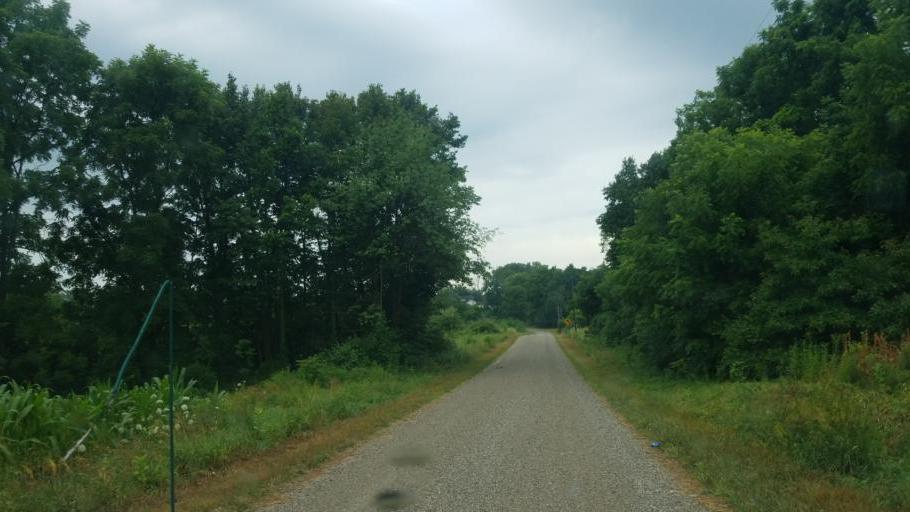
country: US
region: Indiana
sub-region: Steuben County
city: Hamilton
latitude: 41.5078
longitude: -84.9375
